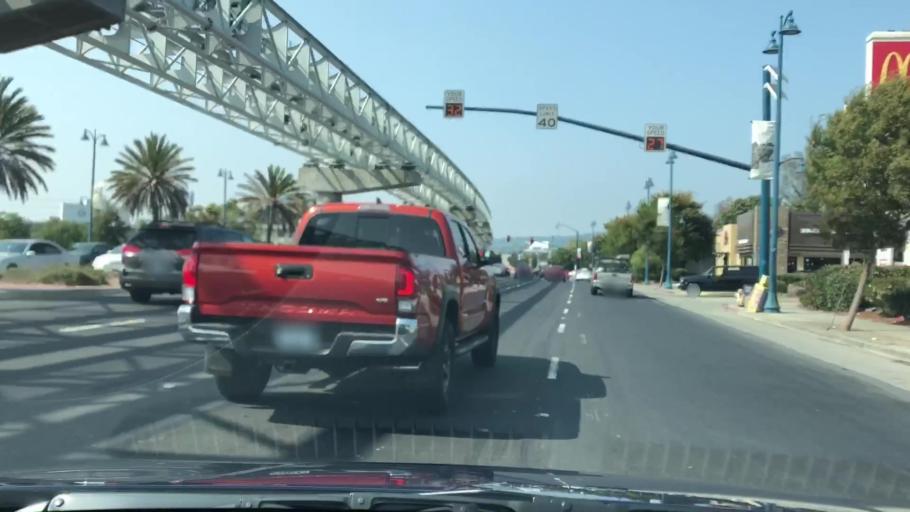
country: US
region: California
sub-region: Alameda County
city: San Leandro
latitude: 37.7461
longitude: -122.1959
